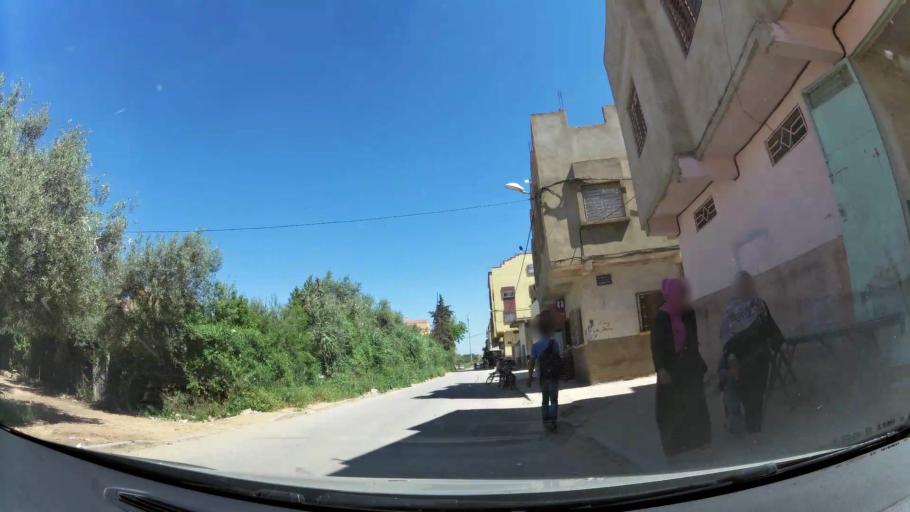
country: MA
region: Meknes-Tafilalet
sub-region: Meknes
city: Meknes
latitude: 33.8666
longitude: -5.5592
